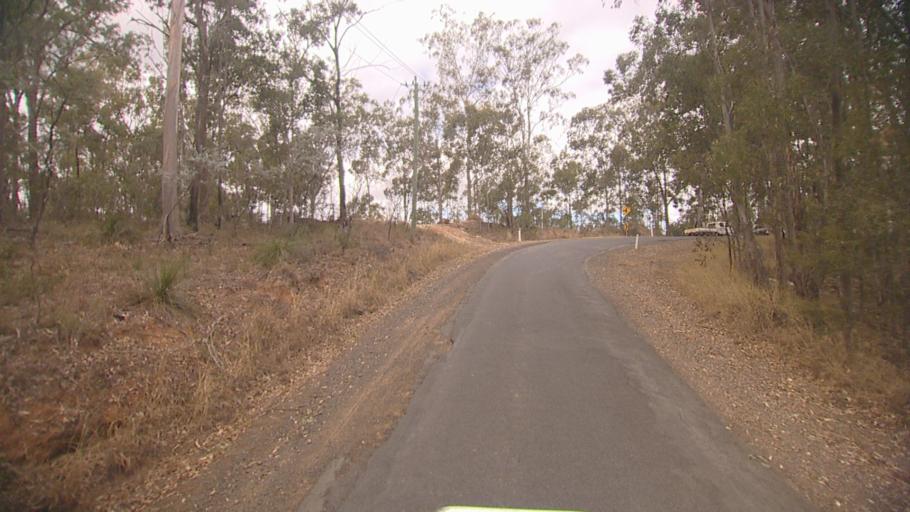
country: AU
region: Queensland
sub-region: Logan
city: Cedar Vale
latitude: -27.8986
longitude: 153.0372
